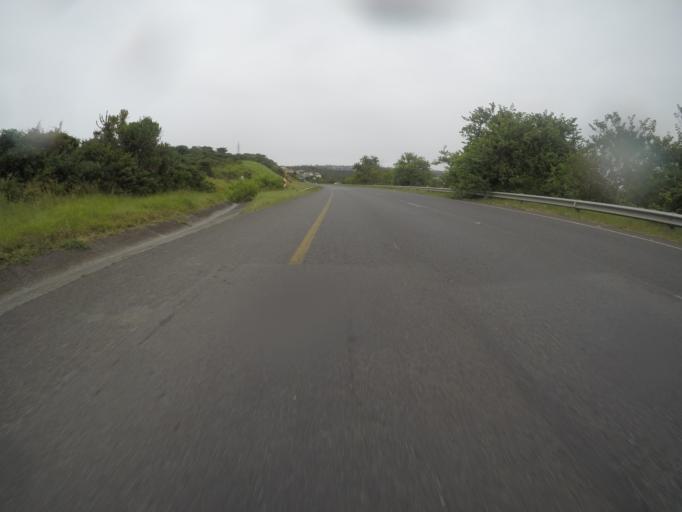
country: ZA
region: Eastern Cape
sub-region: Buffalo City Metropolitan Municipality
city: East London
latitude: -32.9535
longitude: 27.9309
